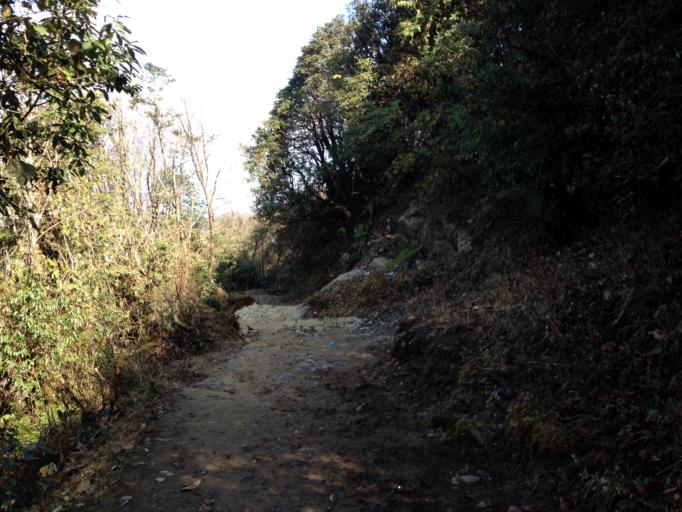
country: NP
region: Central Region
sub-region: Bagmati Zone
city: Nagarkot
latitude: 27.8127
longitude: 85.4377
